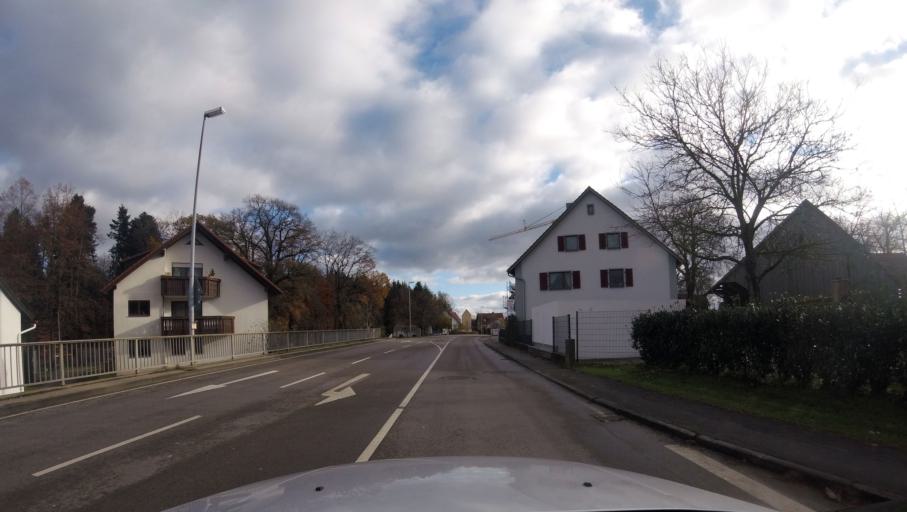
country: DE
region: Baden-Wuerttemberg
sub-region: Regierungsbezirk Stuttgart
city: Gschwend
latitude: 48.9443
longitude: 9.7399
